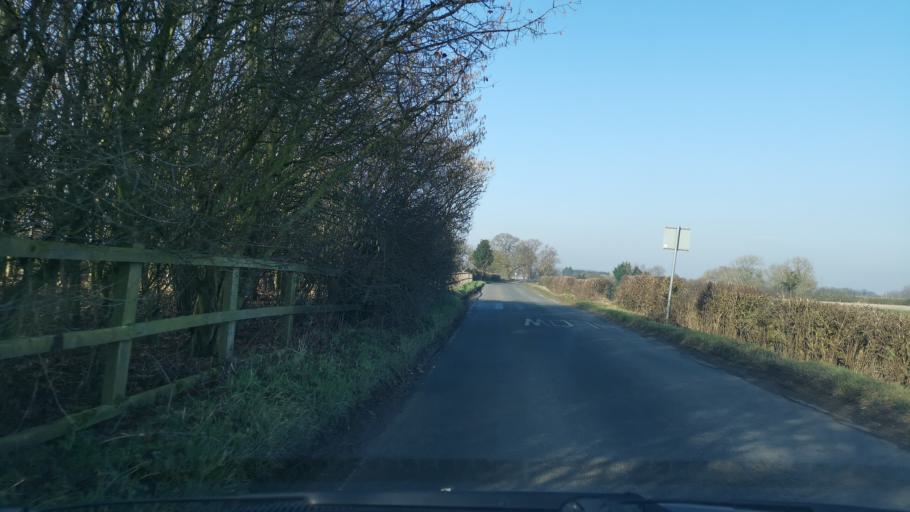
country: GB
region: England
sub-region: City of York
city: Murton
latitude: 53.9692
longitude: -1.0086
